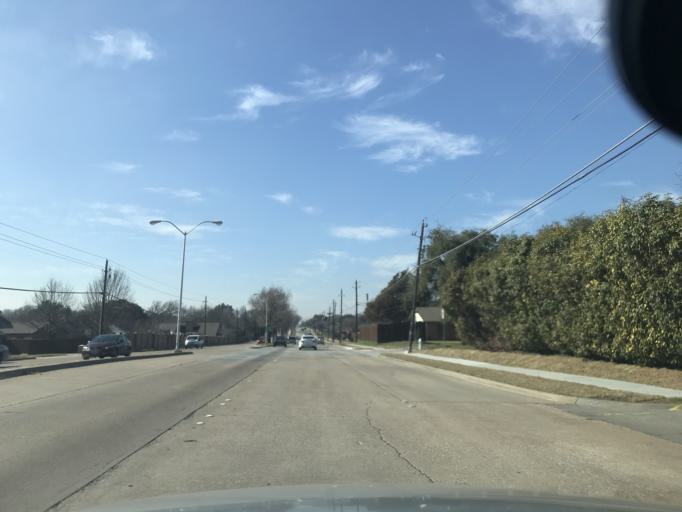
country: US
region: Texas
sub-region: Collin County
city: Plano
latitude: 33.0411
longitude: -96.7199
